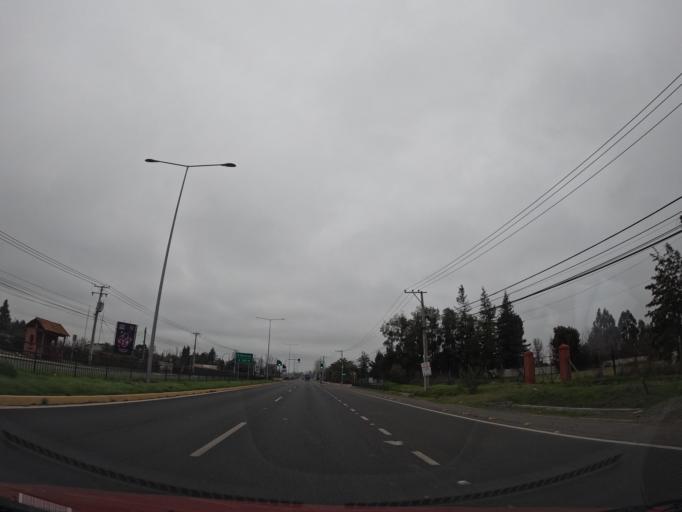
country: CL
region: Maule
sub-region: Provincia de Talca
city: Talca
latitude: -35.4499
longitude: -71.5972
